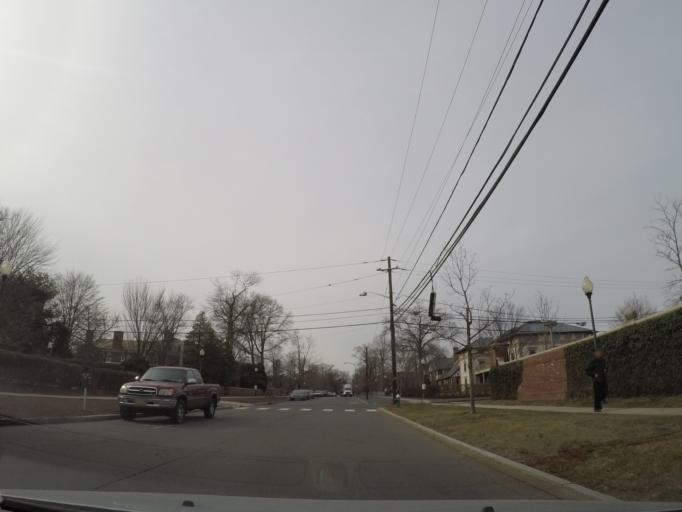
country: US
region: New Jersey
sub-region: Mercer County
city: Princeton
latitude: 40.3490
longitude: -74.6507
